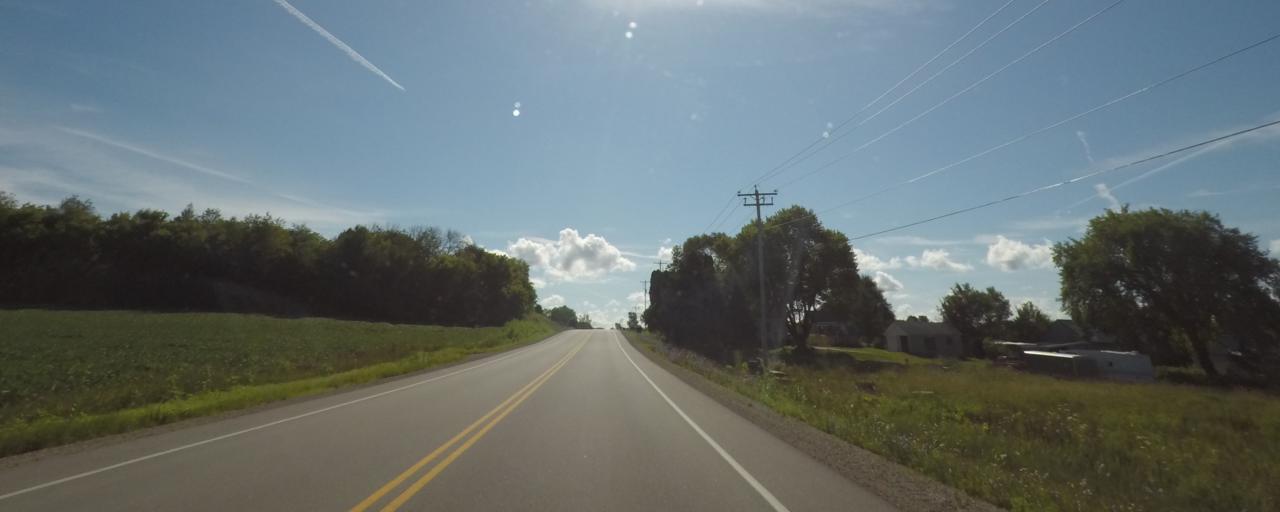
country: US
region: Wisconsin
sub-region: Jefferson County
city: Ixonia
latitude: 43.0733
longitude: -88.6550
